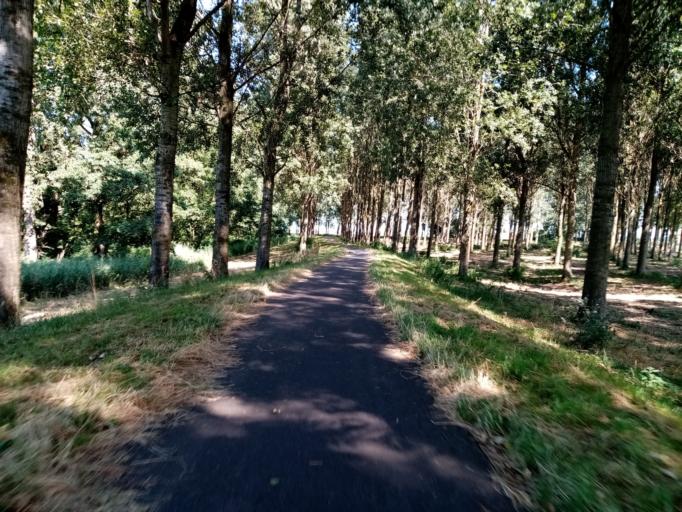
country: NL
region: North Brabant
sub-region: Gemeente Breda
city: Breda
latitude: 51.6287
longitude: 4.6641
